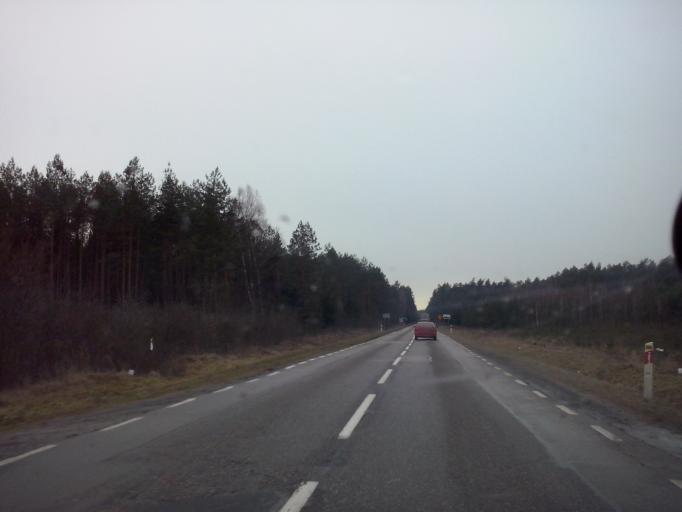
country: PL
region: Lublin Voivodeship
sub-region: Powiat bilgorajski
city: Tereszpol
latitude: 50.6012
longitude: 22.8751
